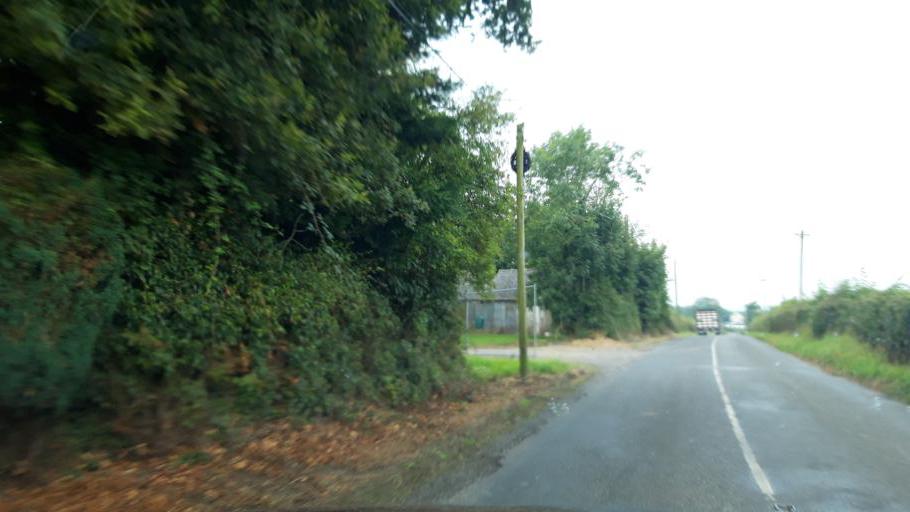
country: IE
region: Leinster
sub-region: Kilkenny
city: Callan
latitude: 52.5119
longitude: -7.4852
